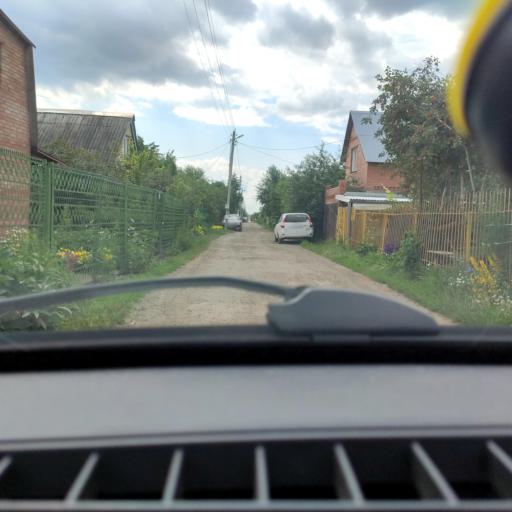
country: RU
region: Samara
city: Podstepki
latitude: 53.6045
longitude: 49.2263
